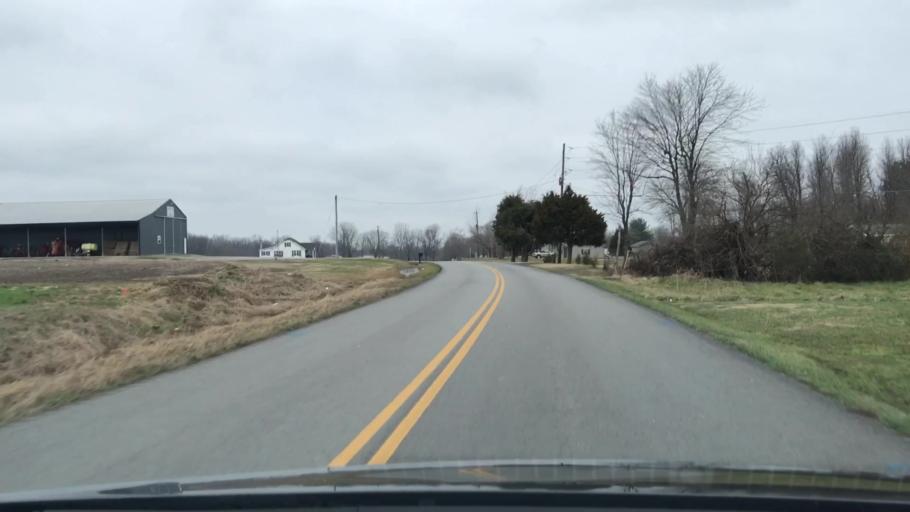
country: US
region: Kentucky
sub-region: Muhlenberg County
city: Morehead
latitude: 37.3345
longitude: -87.2198
